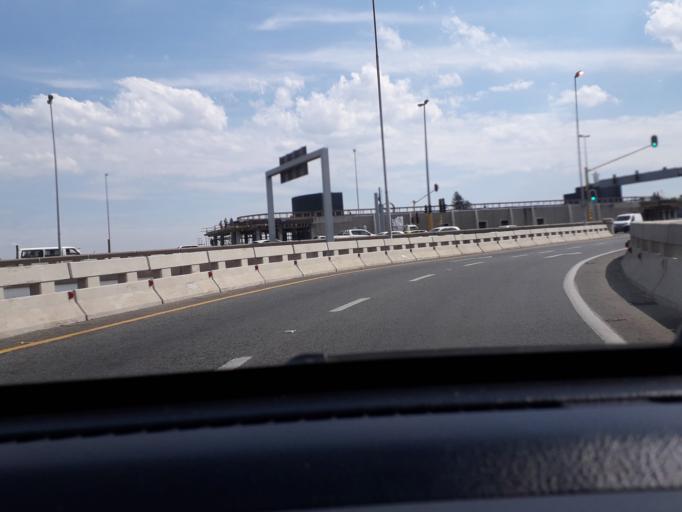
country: ZA
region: Gauteng
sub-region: City of Johannesburg Metropolitan Municipality
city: Midrand
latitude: -25.9798
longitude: 28.1271
